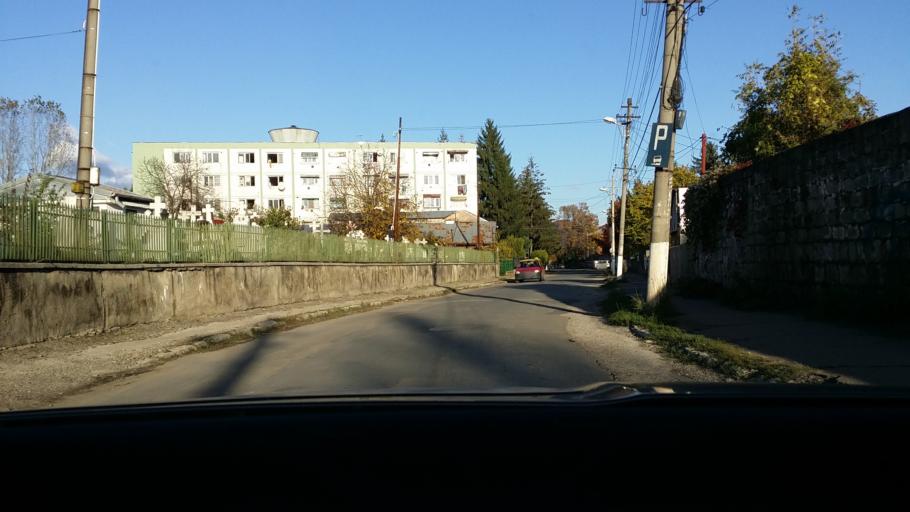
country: RO
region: Prahova
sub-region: Municipiul Campina
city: Campina
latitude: 45.1338
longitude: 25.7399
